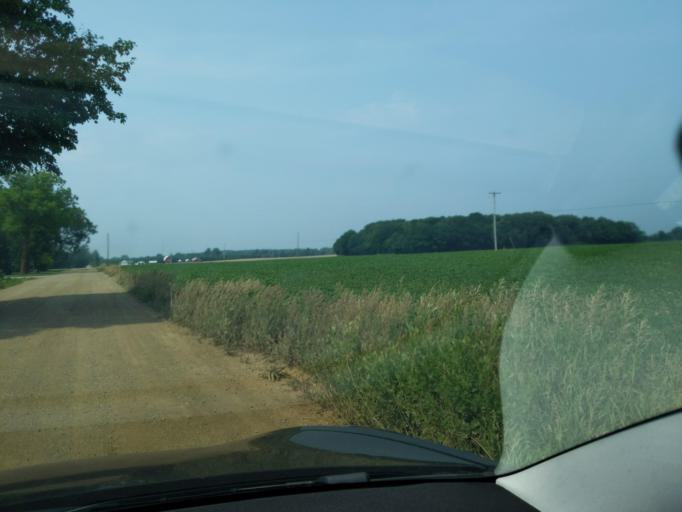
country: US
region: Michigan
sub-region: Clinton County
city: Saint Johns
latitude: 42.9321
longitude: -84.5526
